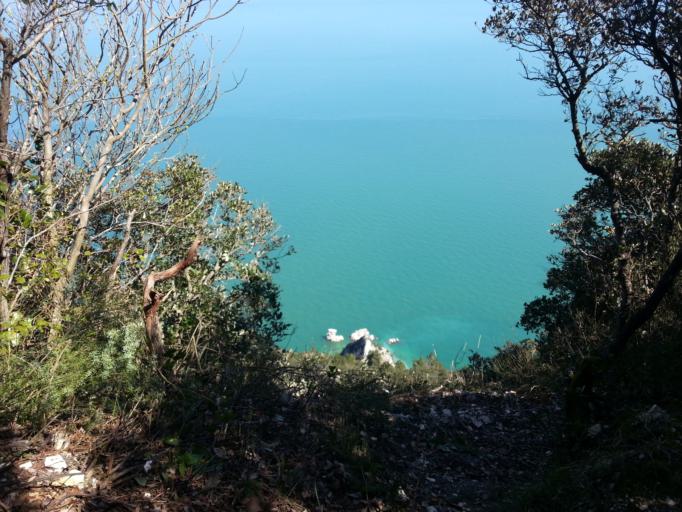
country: IT
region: The Marches
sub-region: Provincia di Ancona
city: Sirolo
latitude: 43.5464
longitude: 13.6200
